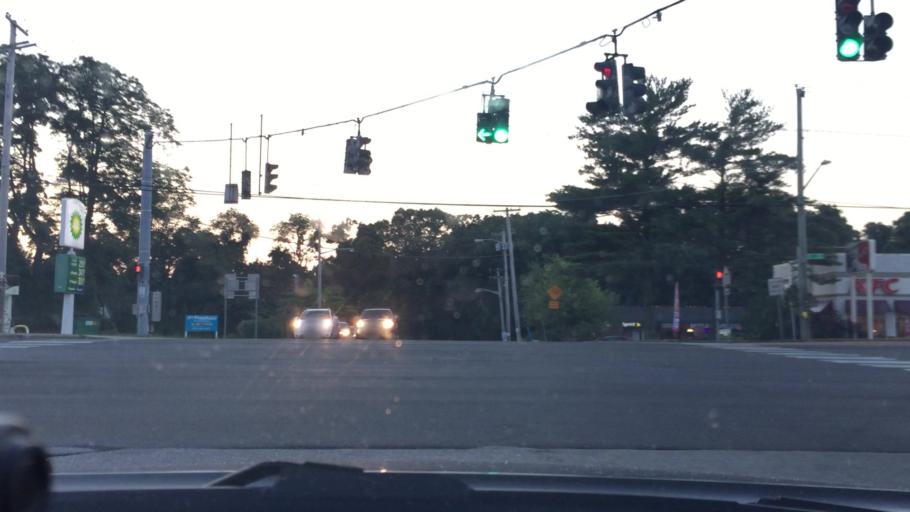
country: US
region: New York
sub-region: Suffolk County
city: Rocky Point
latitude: 40.9451
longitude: -72.9415
